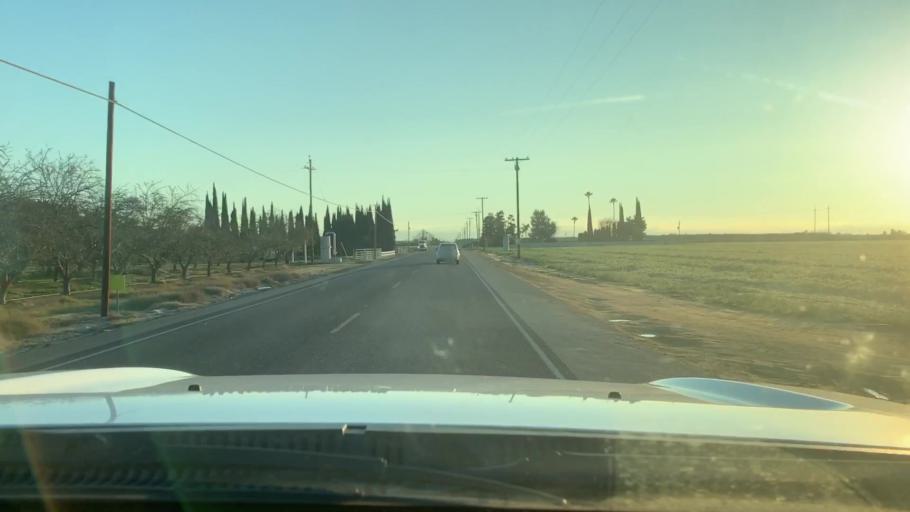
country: US
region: California
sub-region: Kern County
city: Shafter
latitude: 35.5000
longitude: -119.3225
